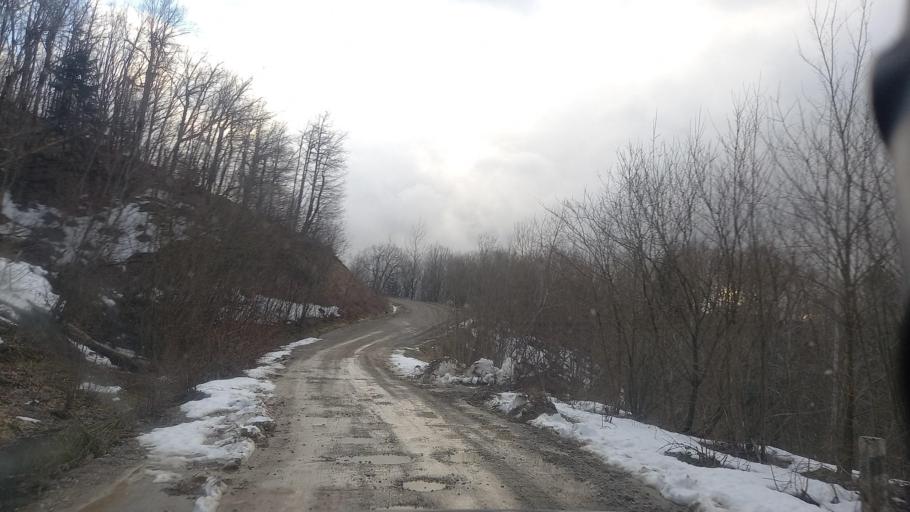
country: RU
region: Krasnodarskiy
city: Dzhubga
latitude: 44.5089
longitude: 38.7697
